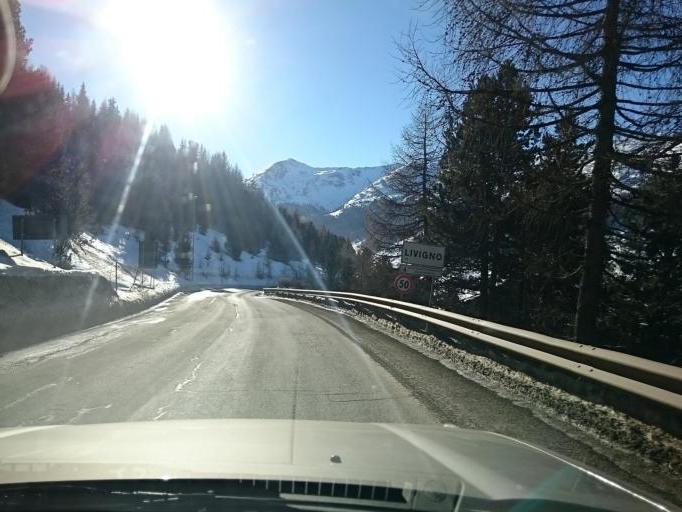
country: IT
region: Lombardy
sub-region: Provincia di Sondrio
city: Livigno
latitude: 46.5317
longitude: 10.1433
